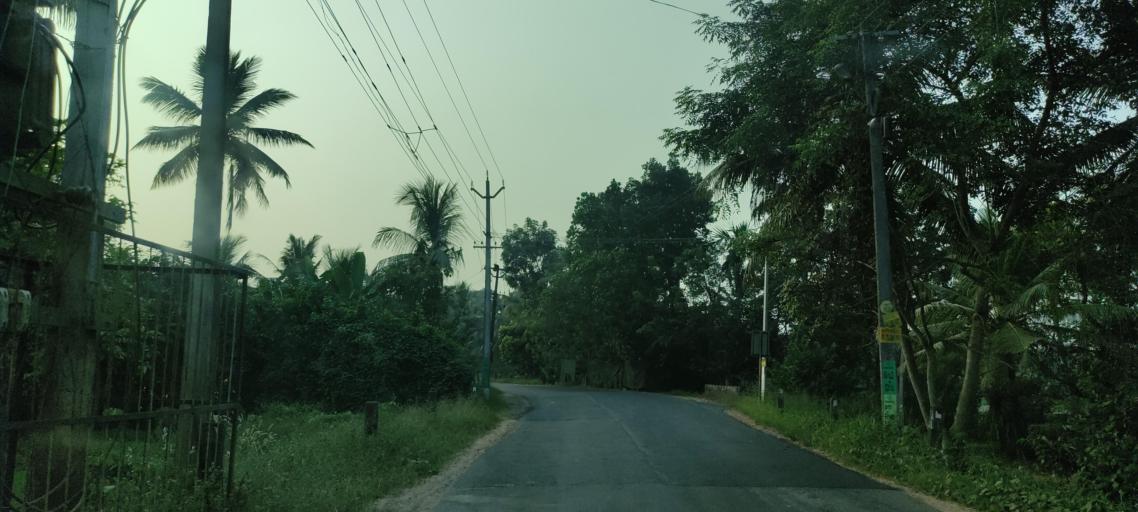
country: IN
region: Kerala
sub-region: Kottayam
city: Vaikam
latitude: 9.6877
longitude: 76.4304
